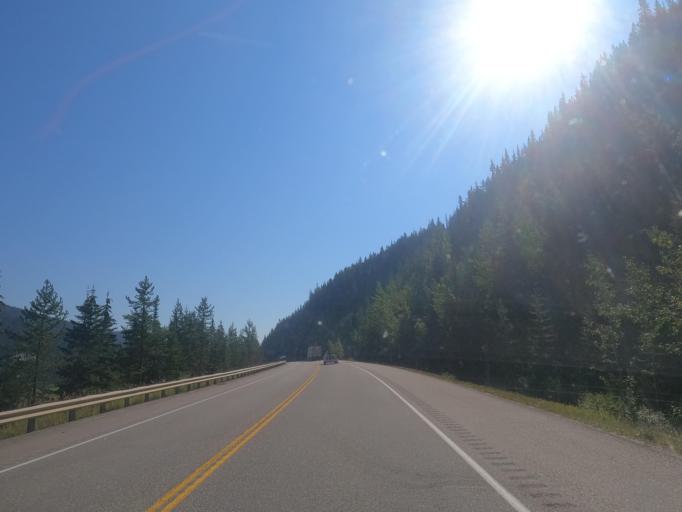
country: CA
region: Alberta
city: Jasper Park Lodge
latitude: 52.8772
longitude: -118.3412
